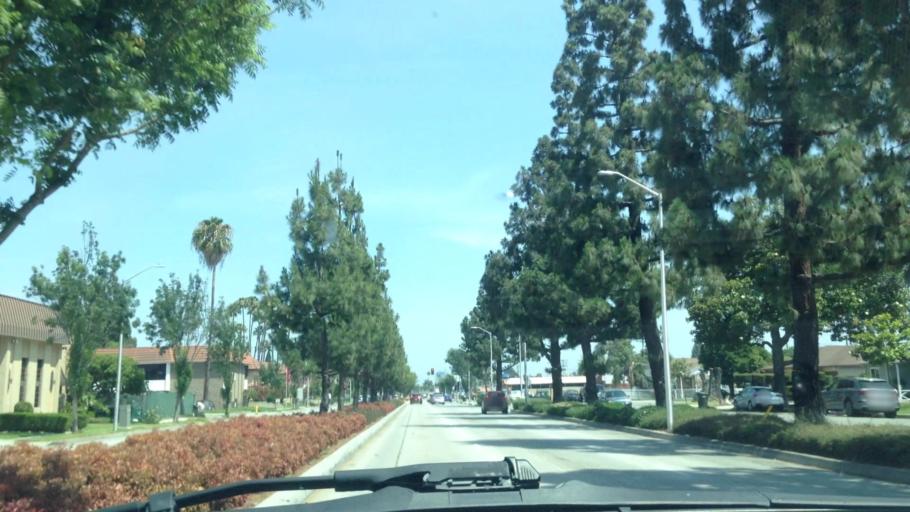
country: US
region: California
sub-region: Los Angeles County
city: Downey
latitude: 33.9192
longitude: -118.1429
